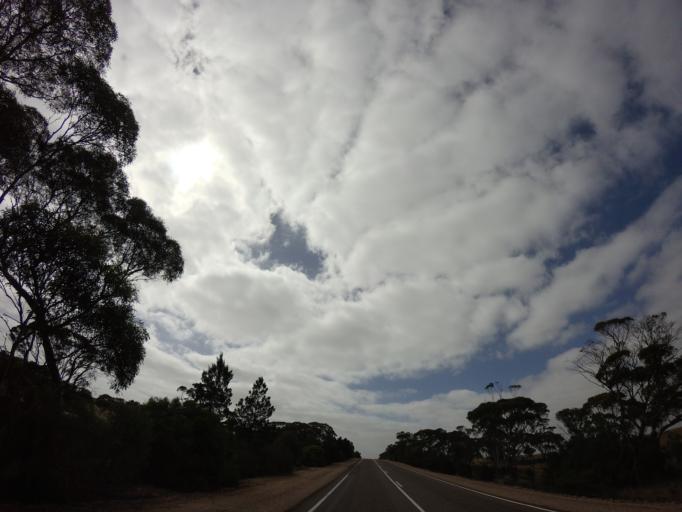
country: AU
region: South Australia
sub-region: Streaky Bay
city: Streaky Bay
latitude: -32.6978
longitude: 134.8117
